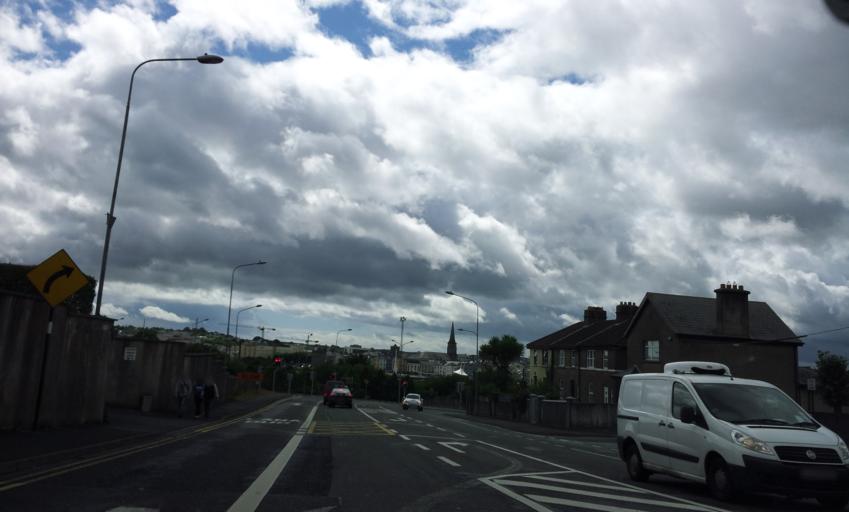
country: IE
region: Munster
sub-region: Waterford
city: Waterford
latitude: 52.2665
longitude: -7.1021
